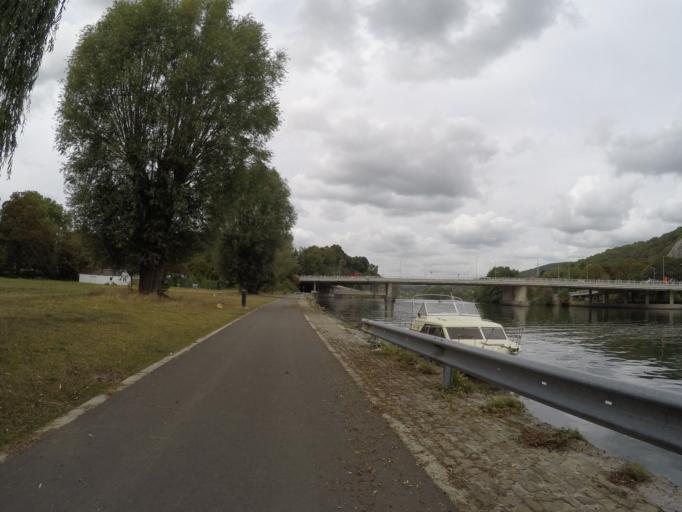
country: BE
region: Wallonia
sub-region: Province de Namur
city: Anhee
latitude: 50.3140
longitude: 4.8779
